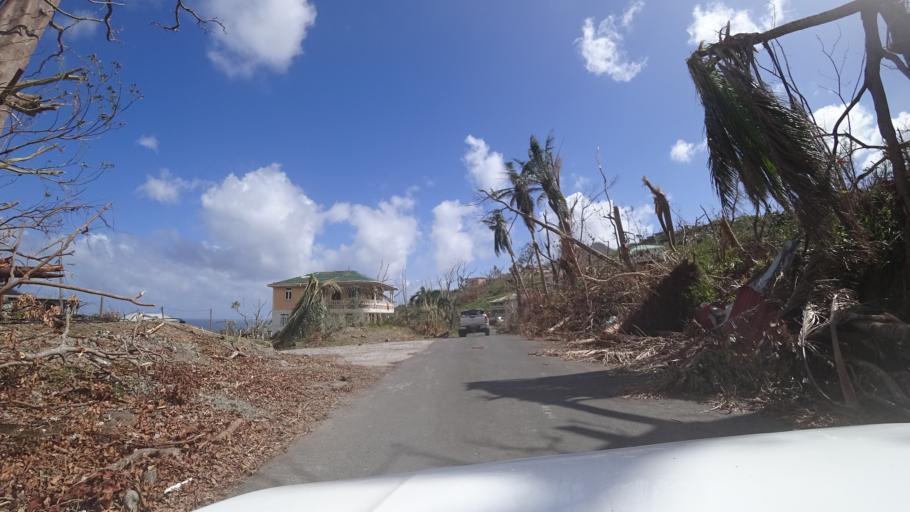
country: DM
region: Saint Patrick
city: Berekua
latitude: 15.2488
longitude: -61.3173
